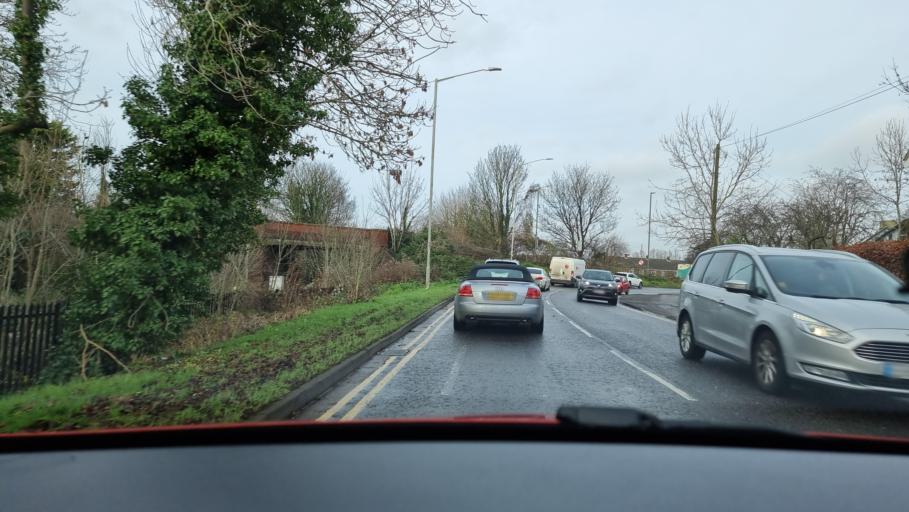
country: GB
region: England
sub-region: Buckinghamshire
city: Aylesbury
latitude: 51.8078
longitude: -0.8099
